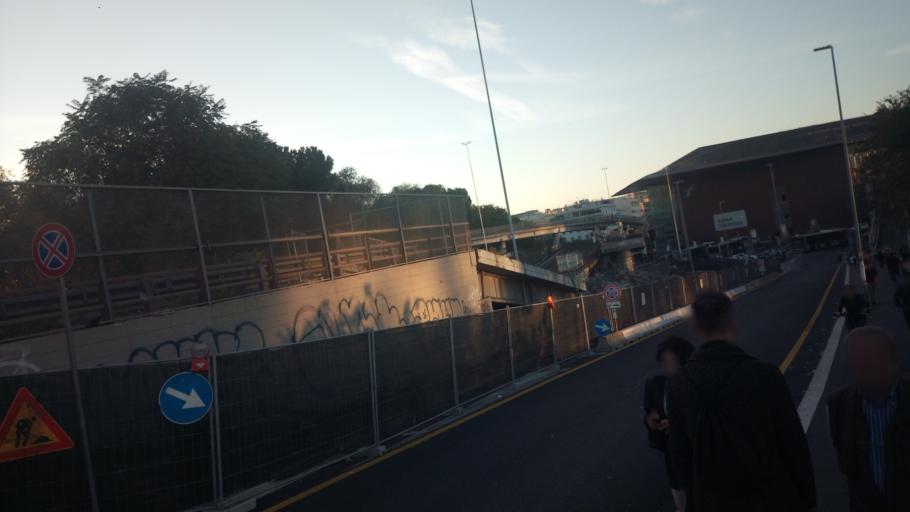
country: IT
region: Latium
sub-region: Citta metropolitana di Roma Capitale
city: Rome
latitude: 41.9085
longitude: 12.5319
